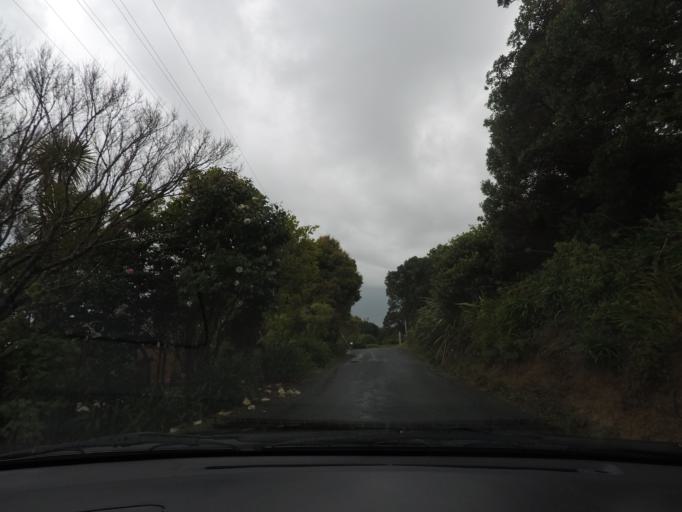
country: NZ
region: Auckland
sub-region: Auckland
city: Warkworth
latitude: -36.4824
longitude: 174.7284
